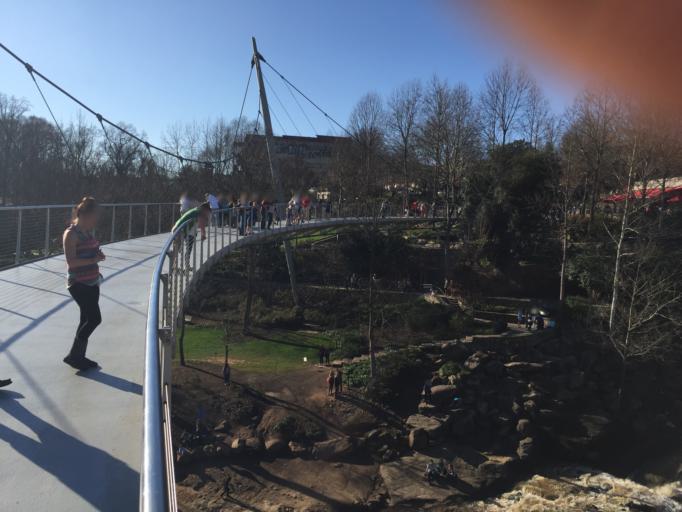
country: US
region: South Carolina
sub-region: Greenville County
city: Greenville
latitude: 34.8446
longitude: -82.4008
